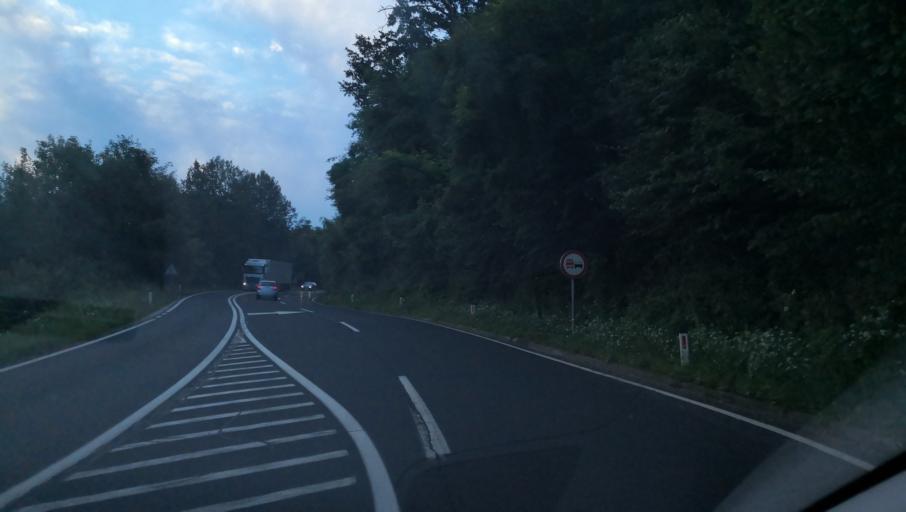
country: SI
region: Novo Mesto
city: Novo Mesto
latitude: 45.7415
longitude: 15.2179
